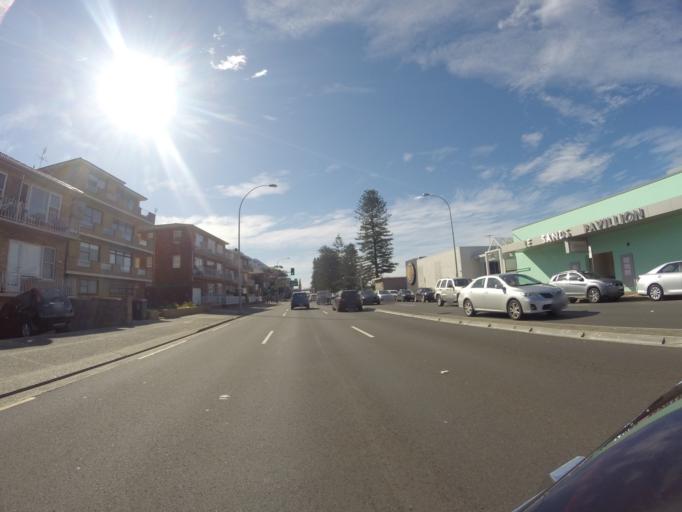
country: AU
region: New South Wales
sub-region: Rockdale
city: Brighton-Le-Sands
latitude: -33.9629
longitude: 151.1554
